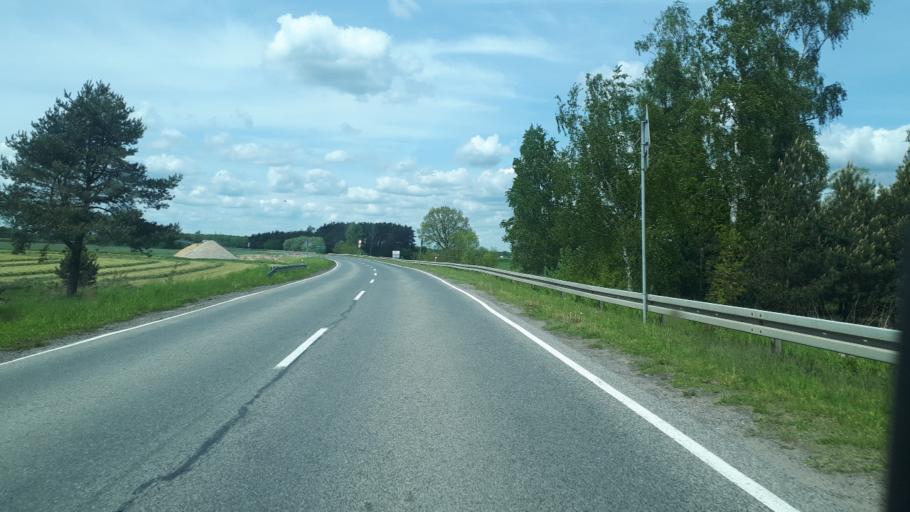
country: PL
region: Silesian Voivodeship
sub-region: Powiat gliwicki
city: Wielowies
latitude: 50.5272
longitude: 18.6047
